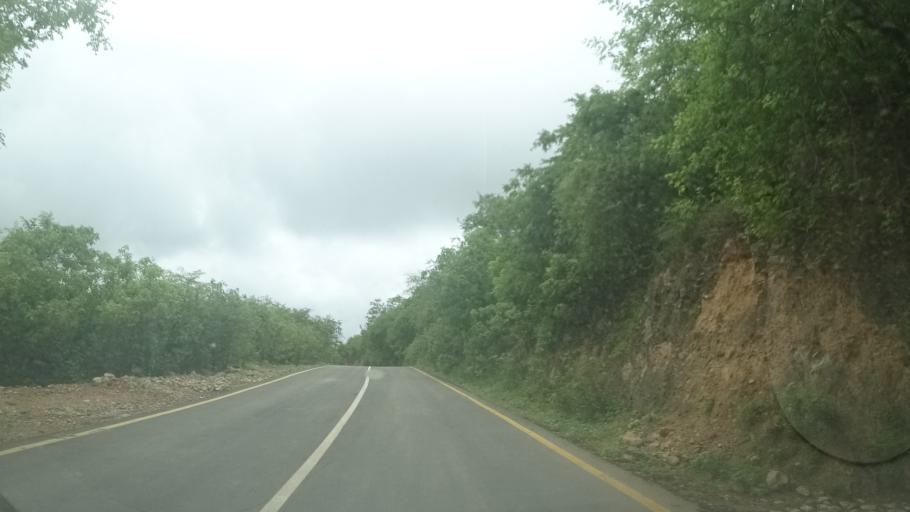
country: OM
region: Zufar
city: Salalah
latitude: 17.1019
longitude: 54.3461
